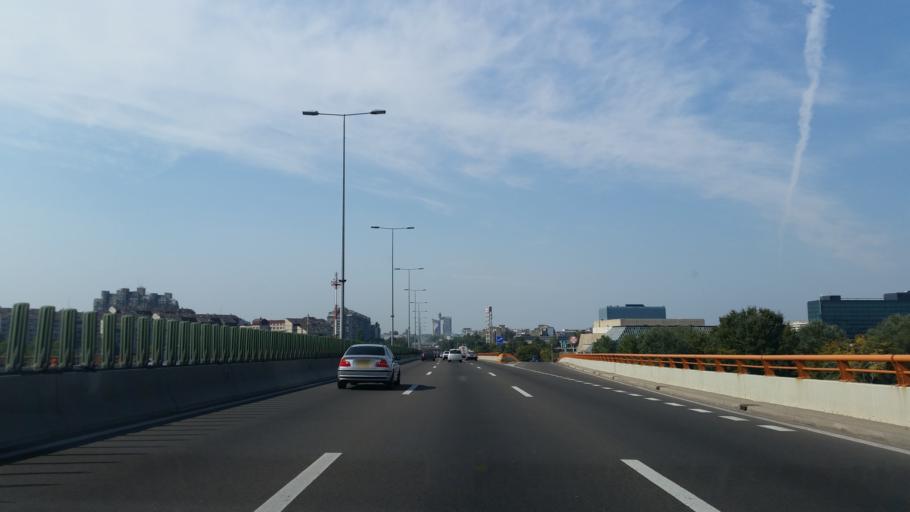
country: RS
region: Central Serbia
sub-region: Belgrade
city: Novi Beograd
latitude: 44.8047
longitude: 20.4372
